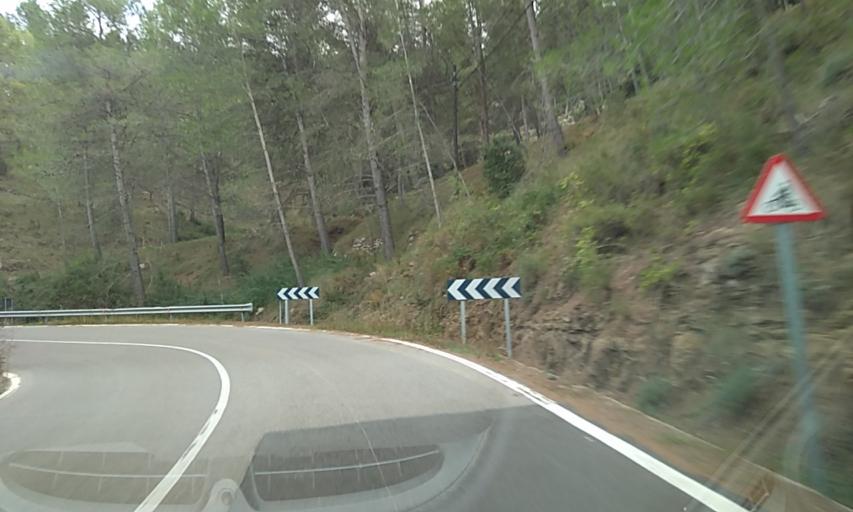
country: ES
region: Valencia
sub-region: Provincia de Castello
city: Puebla de Arenoso
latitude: 40.0877
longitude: -0.5601
